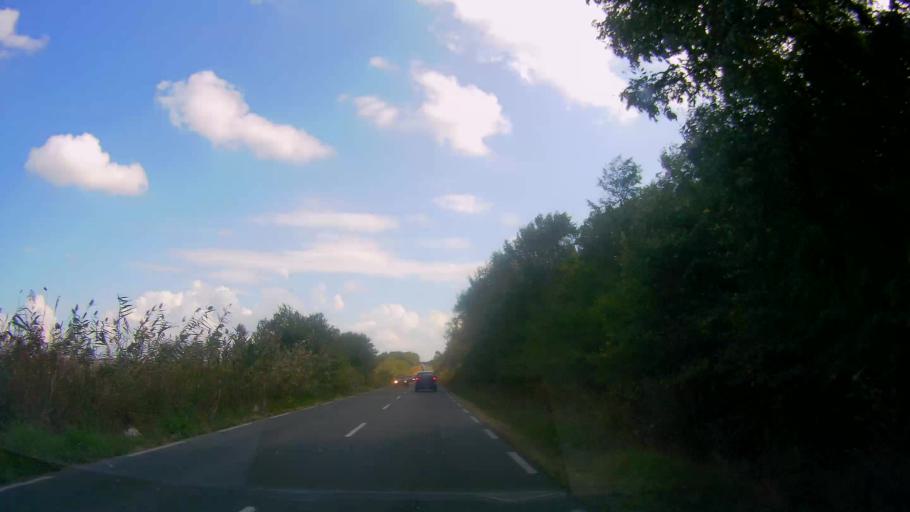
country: BG
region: Burgas
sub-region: Obshtina Kameno
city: Kameno
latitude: 42.4865
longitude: 27.3412
